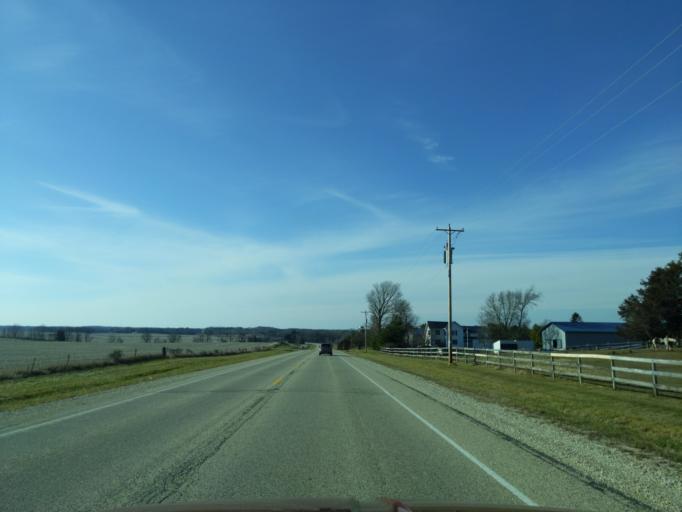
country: US
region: Wisconsin
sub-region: Rock County
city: Milton
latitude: 42.8297
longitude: -88.8613
